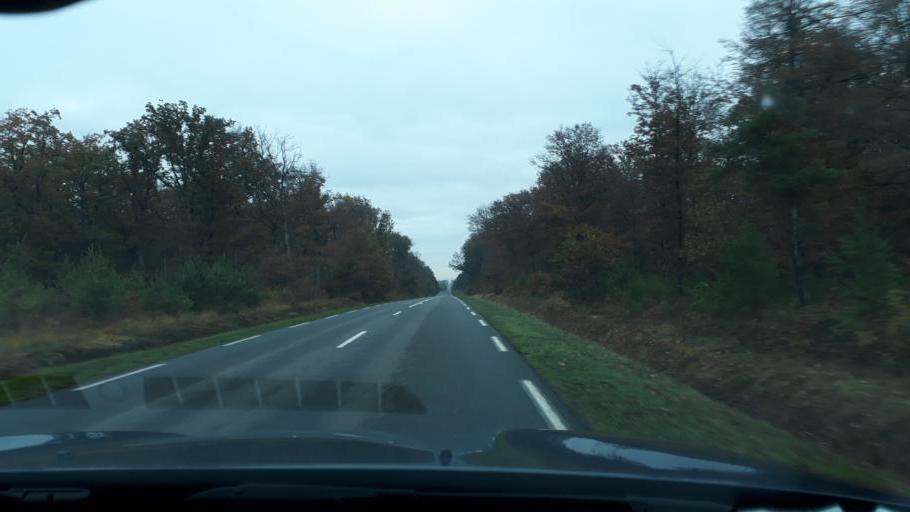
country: FR
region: Centre
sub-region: Departement du Loiret
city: Bouzy-la-Foret
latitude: 47.8331
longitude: 2.4251
